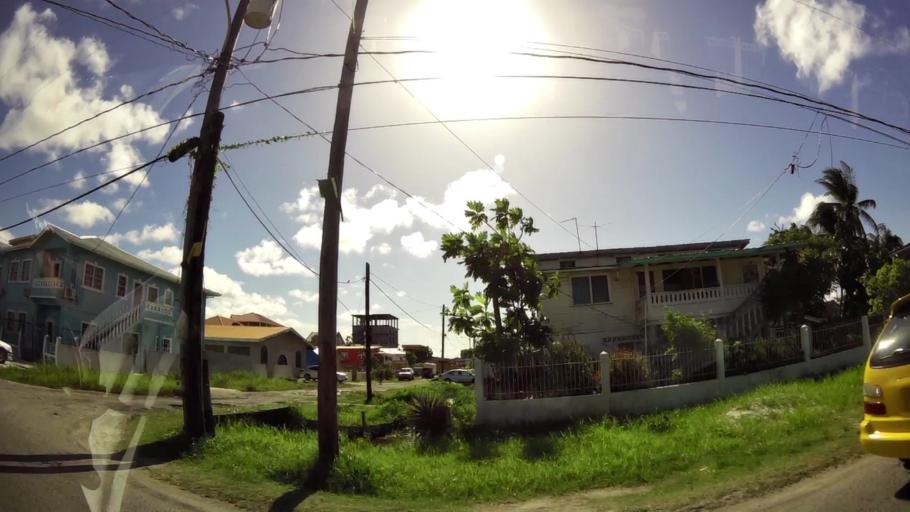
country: GY
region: Demerara-Mahaica
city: Georgetown
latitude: 6.8145
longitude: -58.1343
